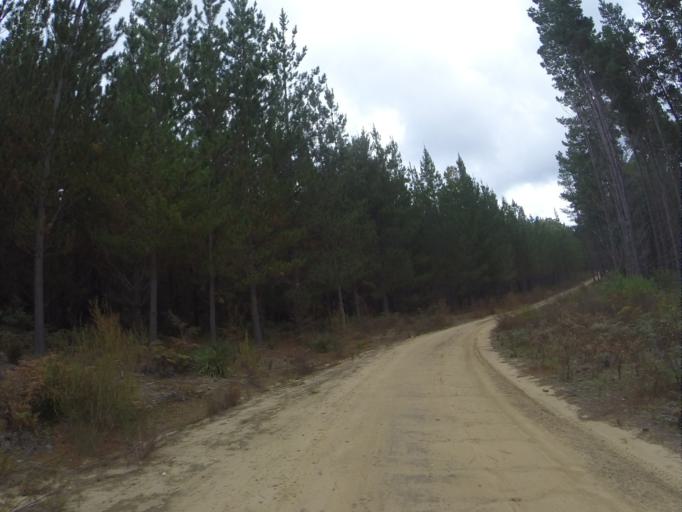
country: AU
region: New South Wales
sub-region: Wingecarribee
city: Moss Vale
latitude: -34.5198
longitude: 150.2467
